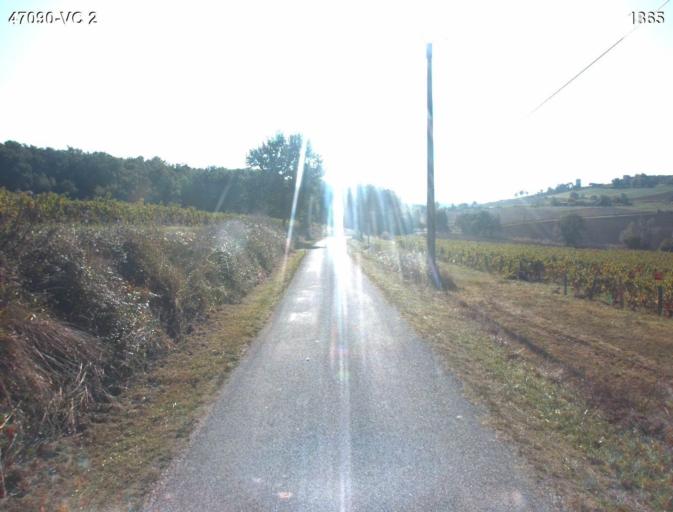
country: FR
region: Aquitaine
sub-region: Departement du Lot-et-Garonne
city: Nerac
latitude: 44.1777
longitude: 0.3746
